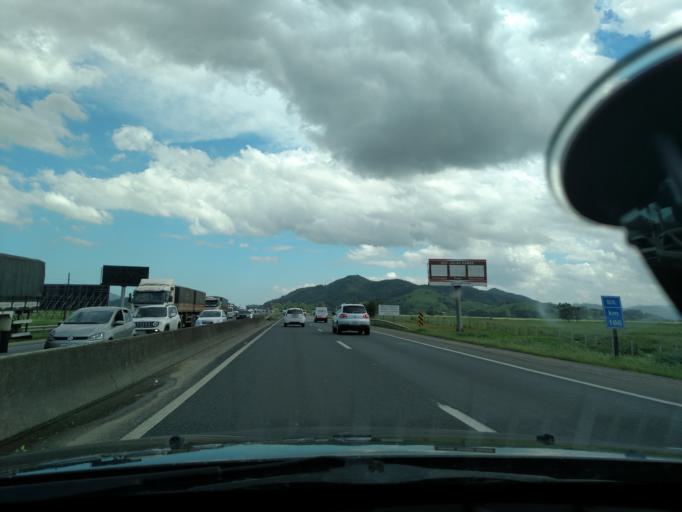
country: BR
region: Santa Catarina
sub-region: Tijucas
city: Tijucas
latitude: -27.2589
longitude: -48.6316
